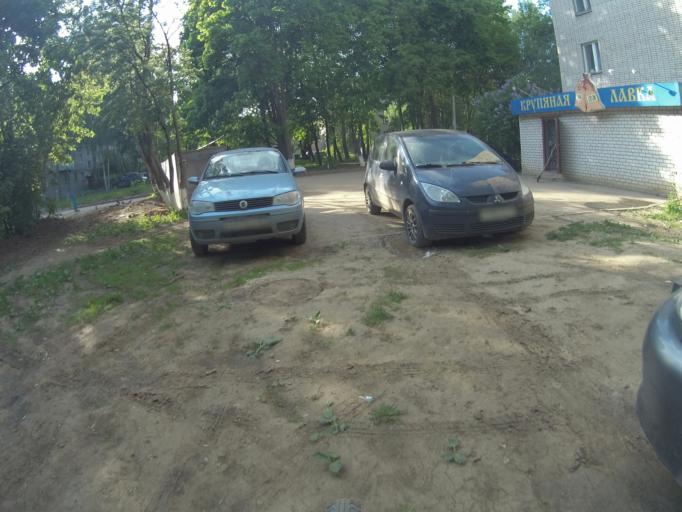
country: RU
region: Vladimir
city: Bogolyubovo
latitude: 56.1673
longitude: 40.4764
